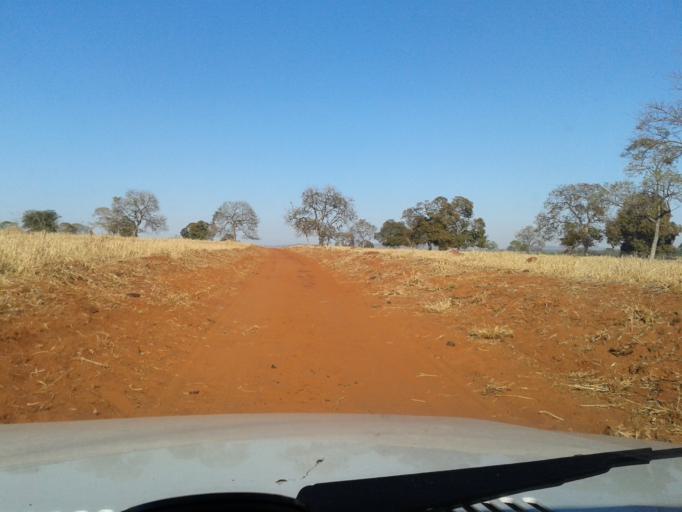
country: BR
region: Minas Gerais
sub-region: Santa Vitoria
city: Santa Vitoria
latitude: -18.9949
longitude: -49.9096
